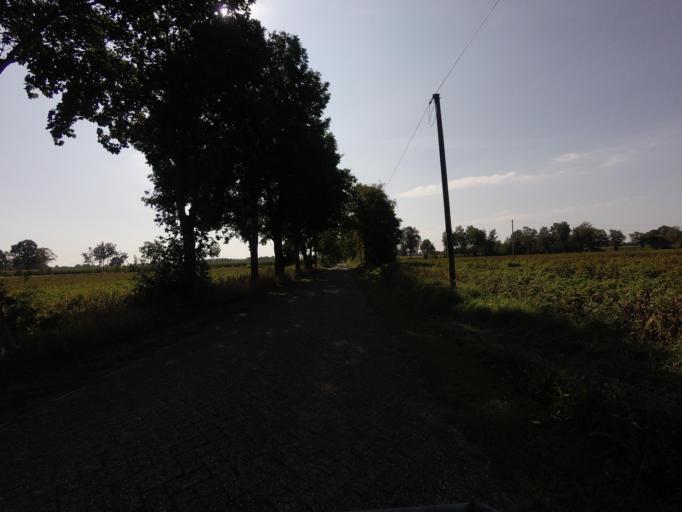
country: DE
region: Lower Saxony
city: Emlichheim
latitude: 52.5806
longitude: 6.8345
